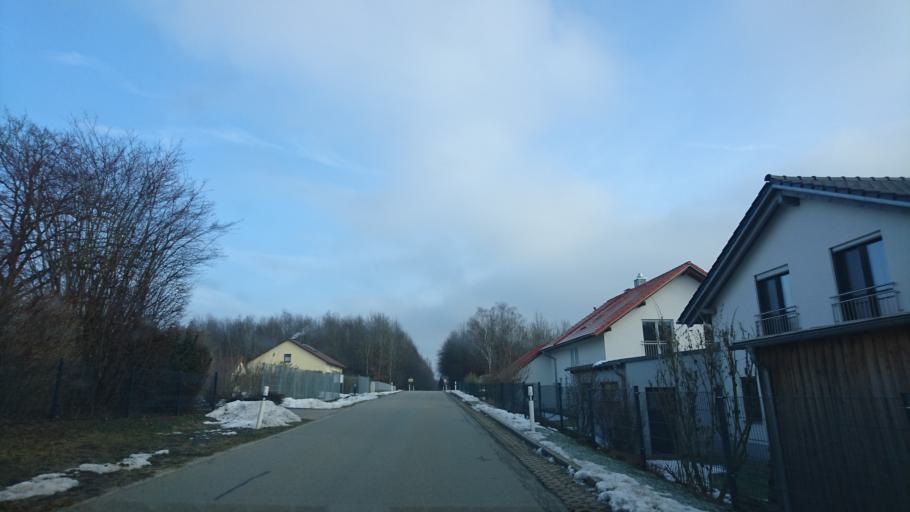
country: DE
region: Bavaria
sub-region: Lower Bavaria
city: Pfarrkirchen
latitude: 48.4412
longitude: 12.9442
